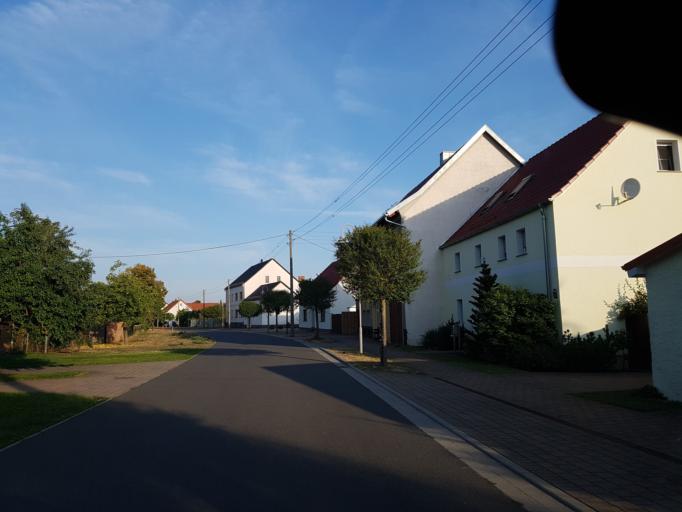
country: DE
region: Saxony-Anhalt
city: Jessen
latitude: 51.8526
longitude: 13.0303
